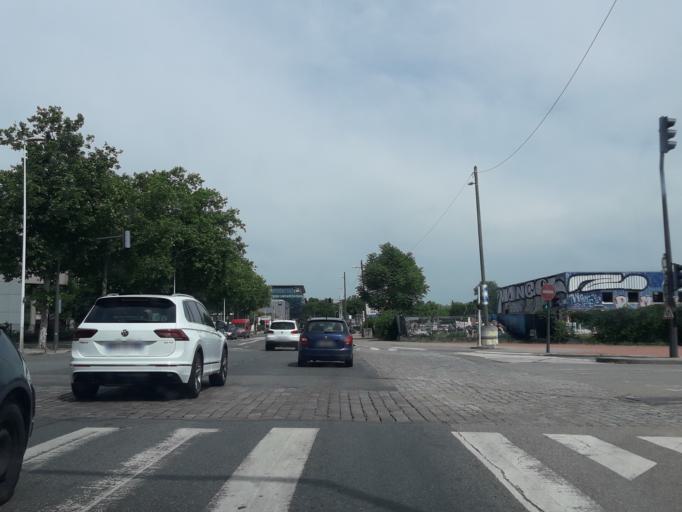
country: FR
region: Rhone-Alpes
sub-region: Departement du Rhone
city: Lyon
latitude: 45.7263
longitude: 4.8353
